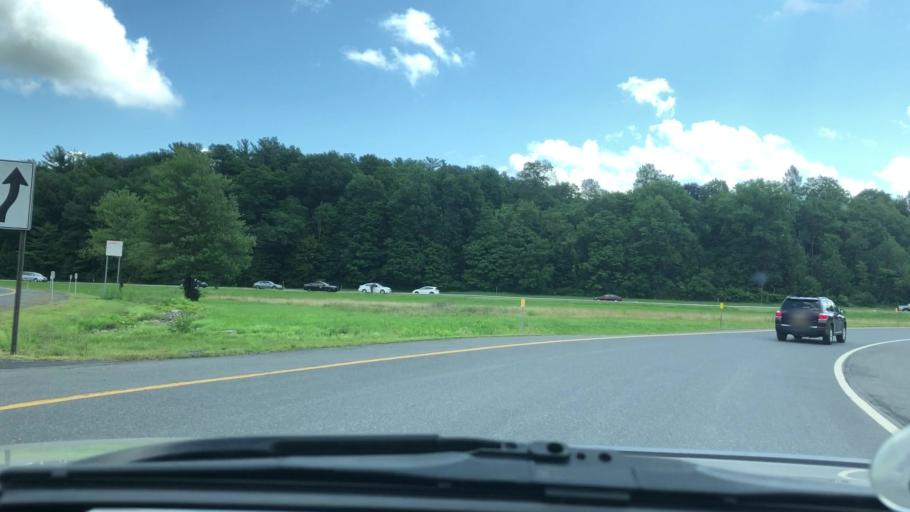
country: US
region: New York
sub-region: Ulster County
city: Saugerties
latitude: 42.0861
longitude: -73.9741
